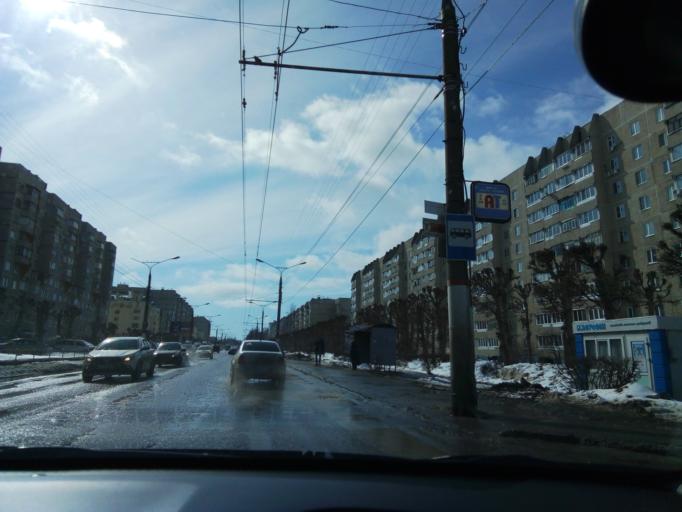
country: RU
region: Chuvashia
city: Novyye Lapsary
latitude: 56.1166
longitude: 47.1914
